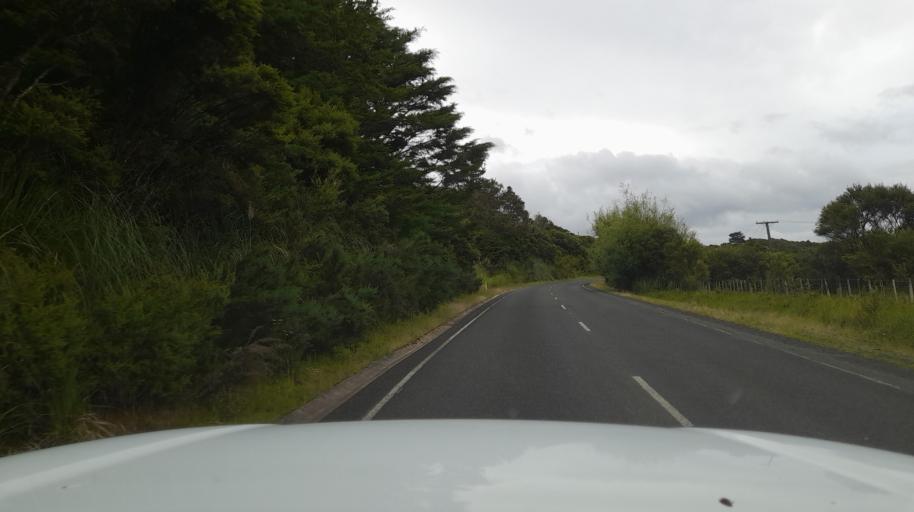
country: NZ
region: Northland
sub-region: Far North District
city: Kaitaia
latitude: -35.3605
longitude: 173.4022
